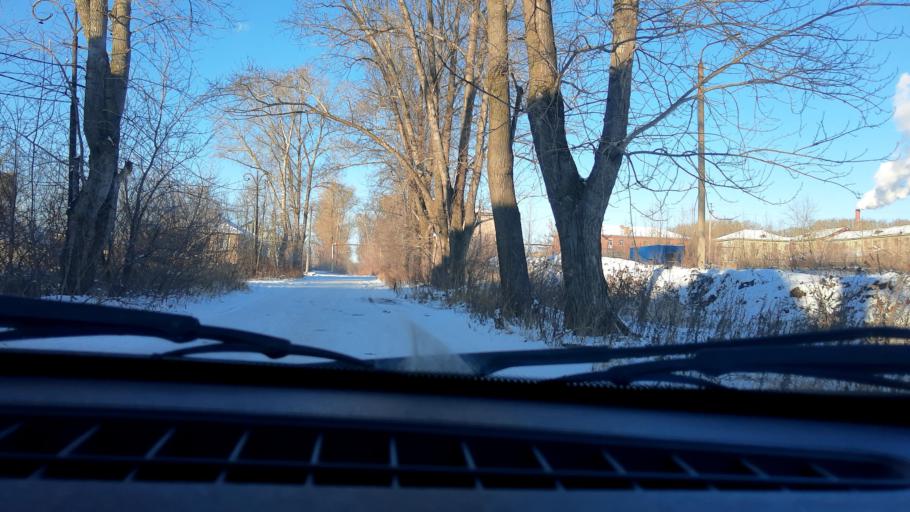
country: RU
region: Bashkortostan
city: Blagoveshchensk
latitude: 54.8983
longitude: 56.0568
